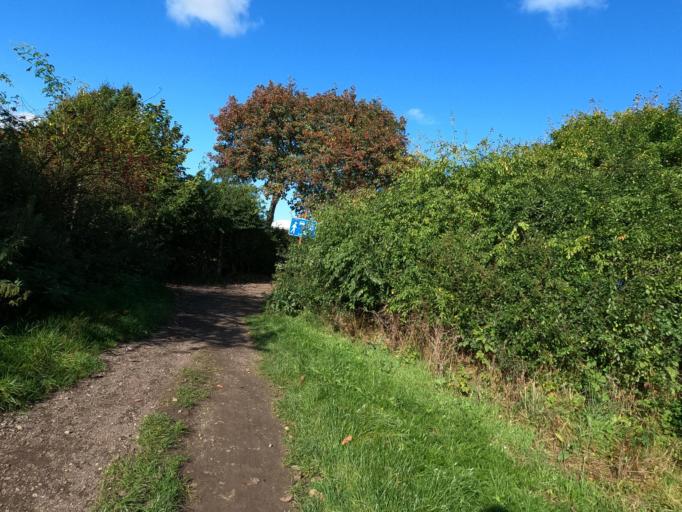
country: DE
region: Schleswig-Holstein
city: Neukirchen
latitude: 54.3195
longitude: 11.0732
